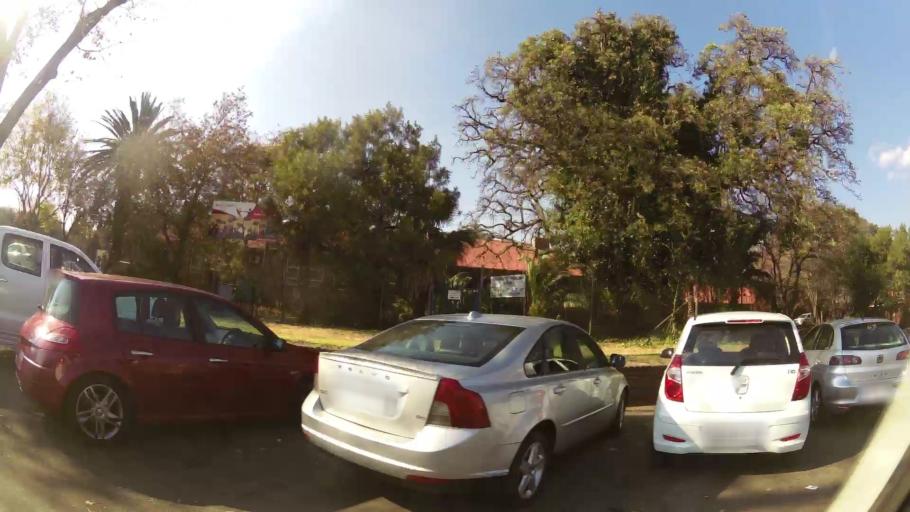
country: ZA
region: Gauteng
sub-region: Ekurhuleni Metropolitan Municipality
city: Germiston
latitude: -26.1797
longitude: 28.1377
